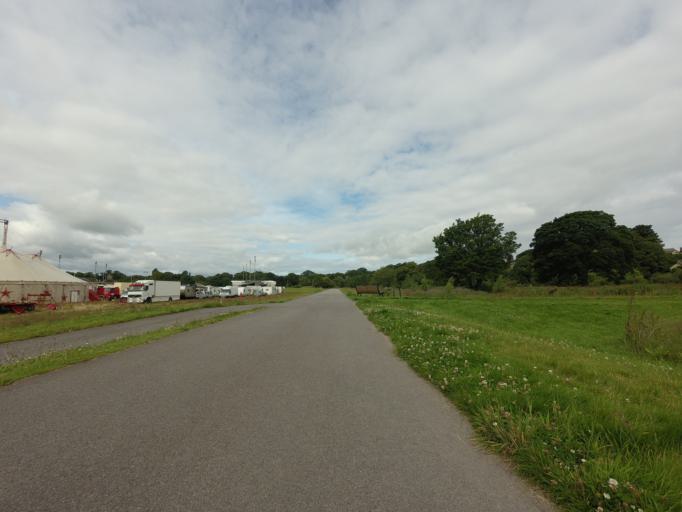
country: GB
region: Scotland
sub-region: Moray
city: Elgin
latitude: 57.6526
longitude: -3.3180
